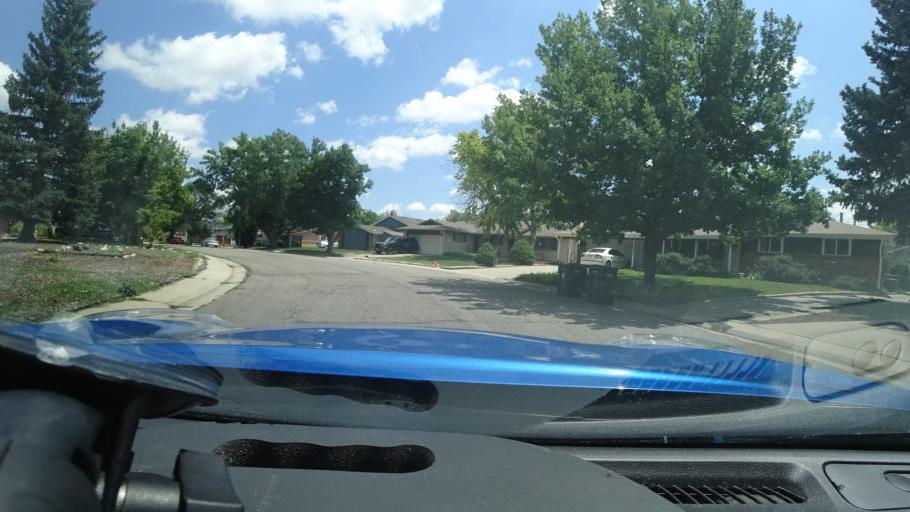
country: US
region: Colorado
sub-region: Adams County
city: Aurora
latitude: 39.7088
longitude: -104.8401
